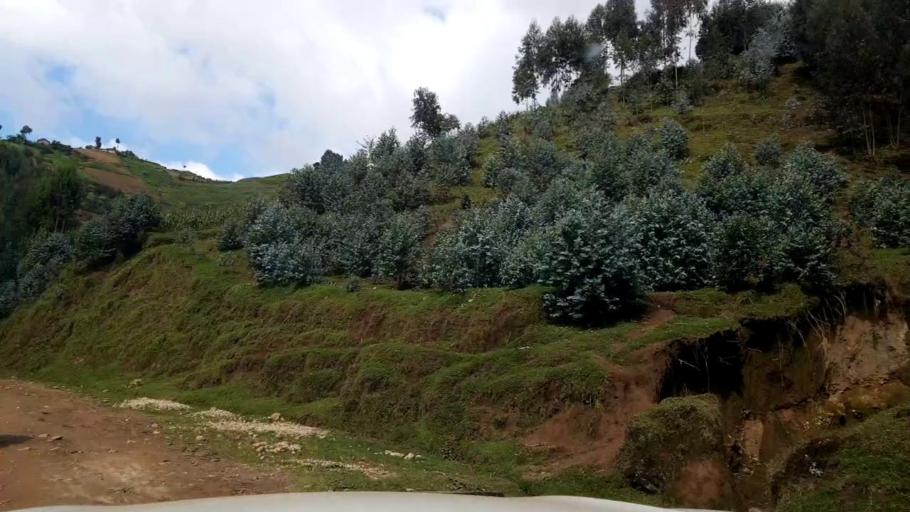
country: RW
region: Western Province
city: Kibuye
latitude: -1.8871
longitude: 29.4685
